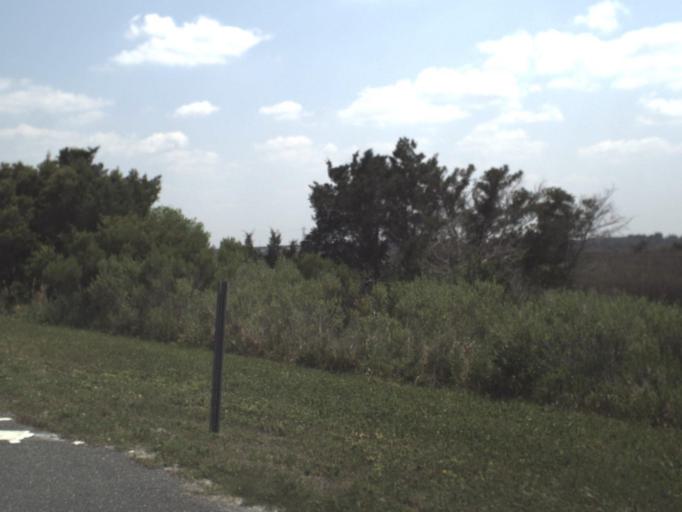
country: US
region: Florida
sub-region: Duval County
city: Atlantic Beach
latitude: 30.3756
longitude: -81.4361
